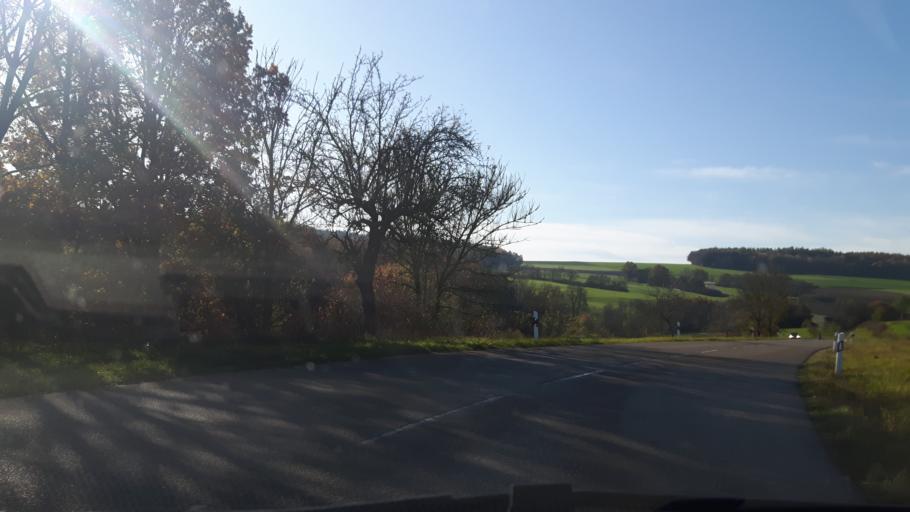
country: DE
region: Bavaria
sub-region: Swabia
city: Marxheim
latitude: 48.7751
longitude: 10.9596
